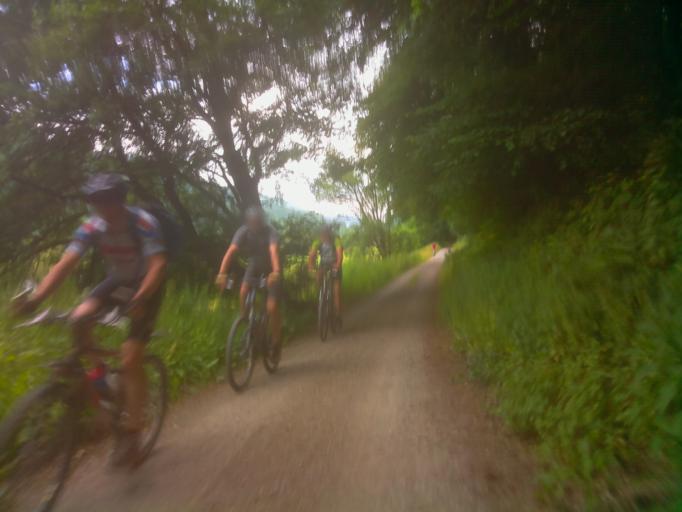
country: DE
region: Hesse
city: Hirschhorn
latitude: 49.4264
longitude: 8.8951
